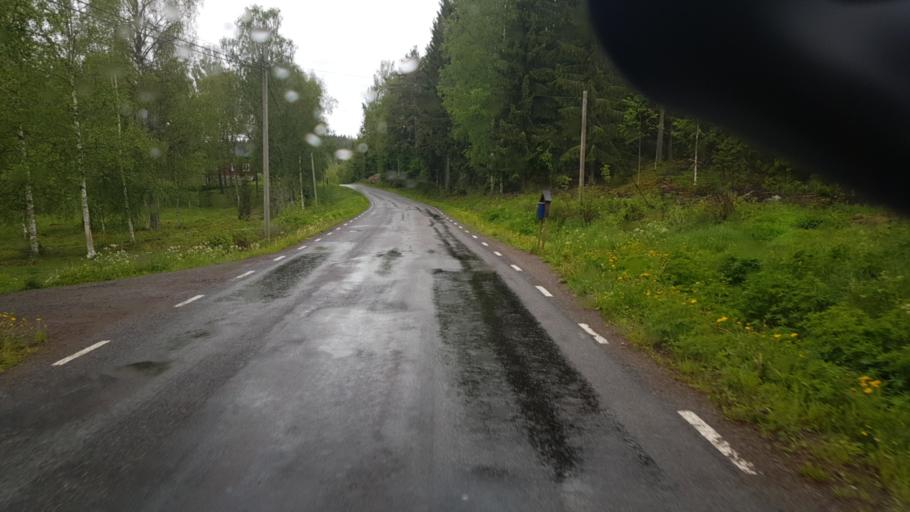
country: SE
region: Vaermland
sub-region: Eda Kommun
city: Amotfors
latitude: 59.8633
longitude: 12.4264
